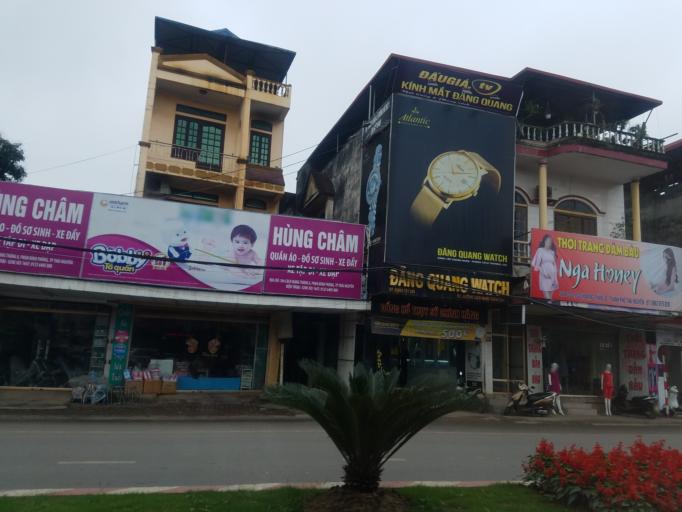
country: VN
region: Thai Nguyen
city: Thanh Pho Thai Nguyen
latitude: 21.5921
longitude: 105.8434
